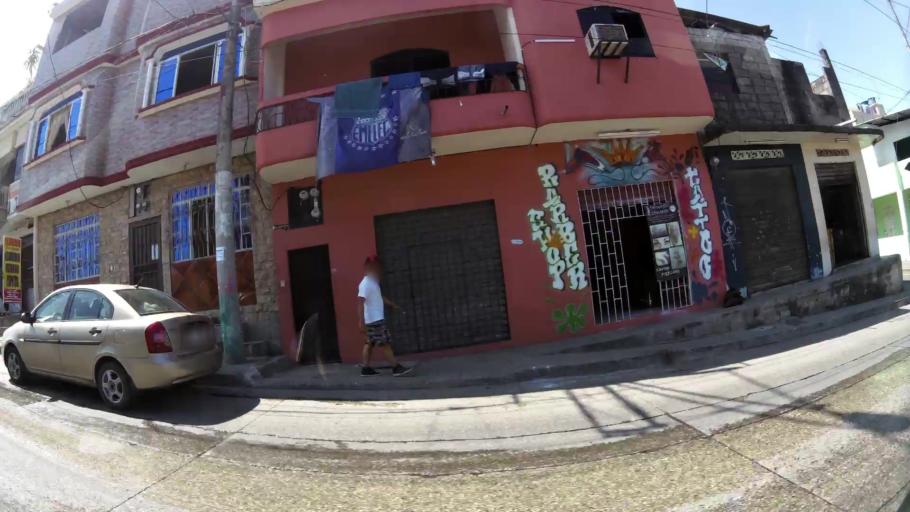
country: EC
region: Guayas
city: Guayaquil
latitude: -2.1307
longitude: -79.9198
